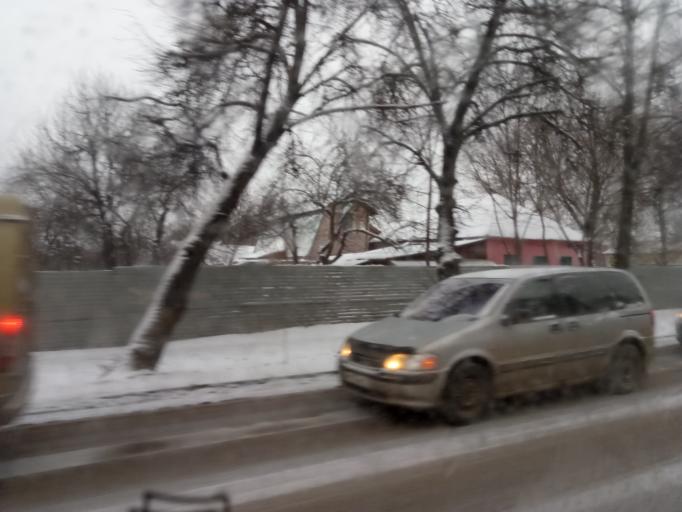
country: RU
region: Tula
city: Mendeleyevskiy
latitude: 54.1658
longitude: 37.5913
